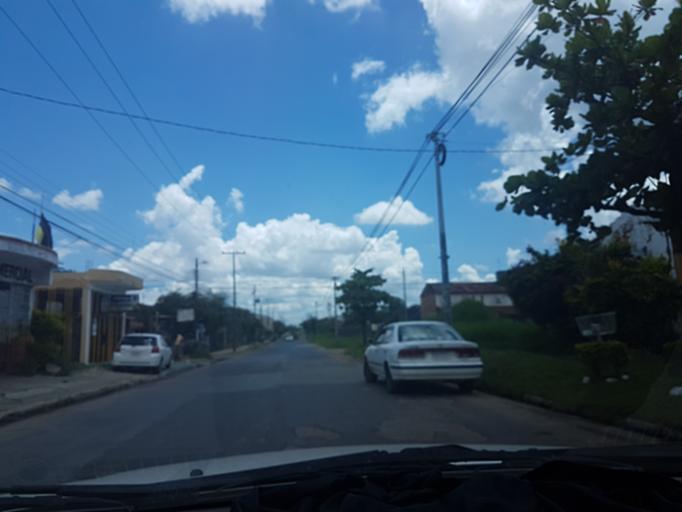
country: PY
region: Central
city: Fernando de la Mora
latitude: -25.2837
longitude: -57.5373
